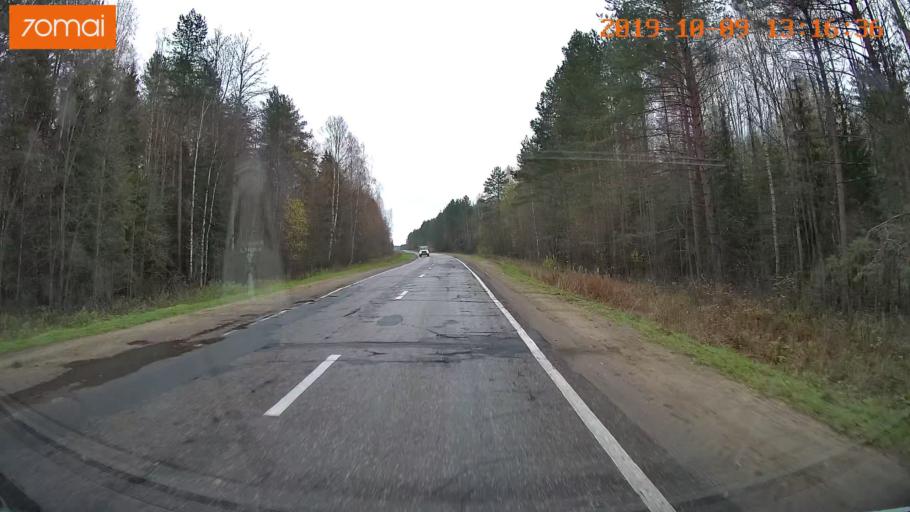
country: RU
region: Jaroslavl
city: Lyubim
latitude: 58.3600
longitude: 40.7680
